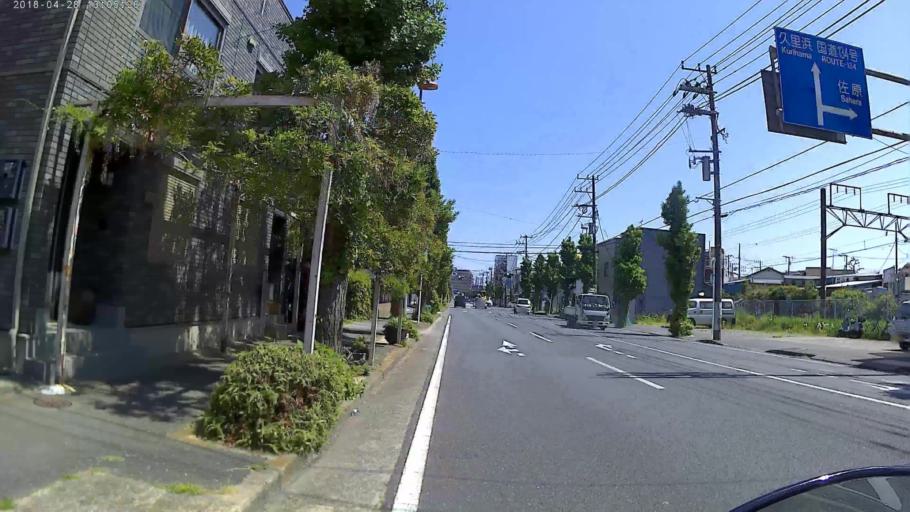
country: JP
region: Kanagawa
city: Yokosuka
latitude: 35.2494
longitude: 139.6808
